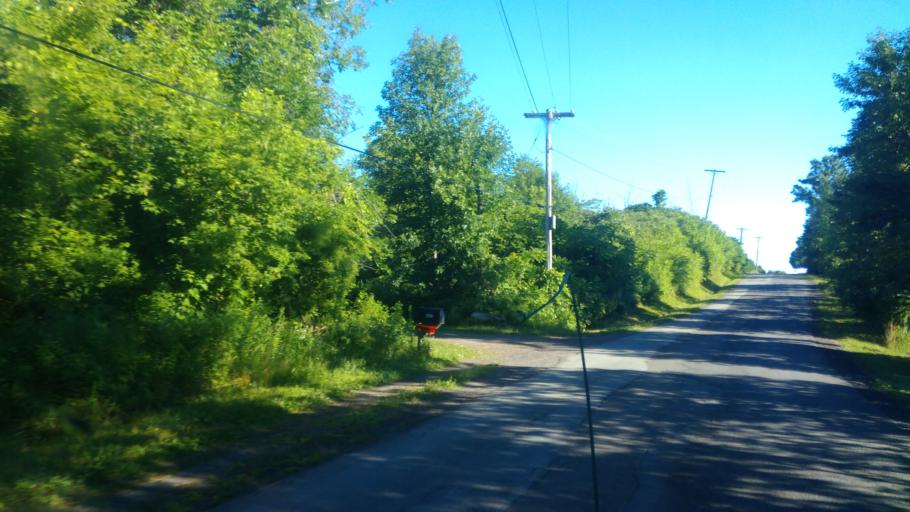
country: US
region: New York
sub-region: Wayne County
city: Sodus
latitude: 43.1732
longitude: -77.0615
